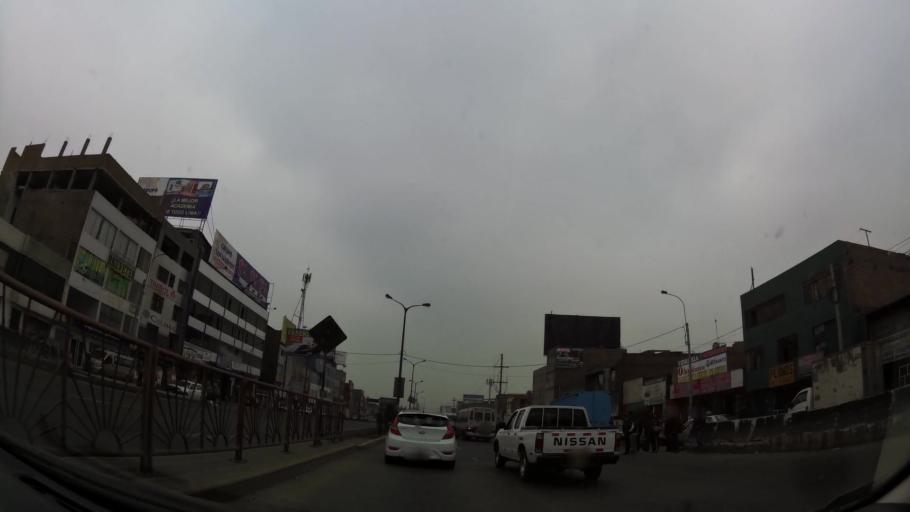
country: PE
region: Lima
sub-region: Lima
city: Vitarte
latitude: -12.0348
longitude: -76.9292
